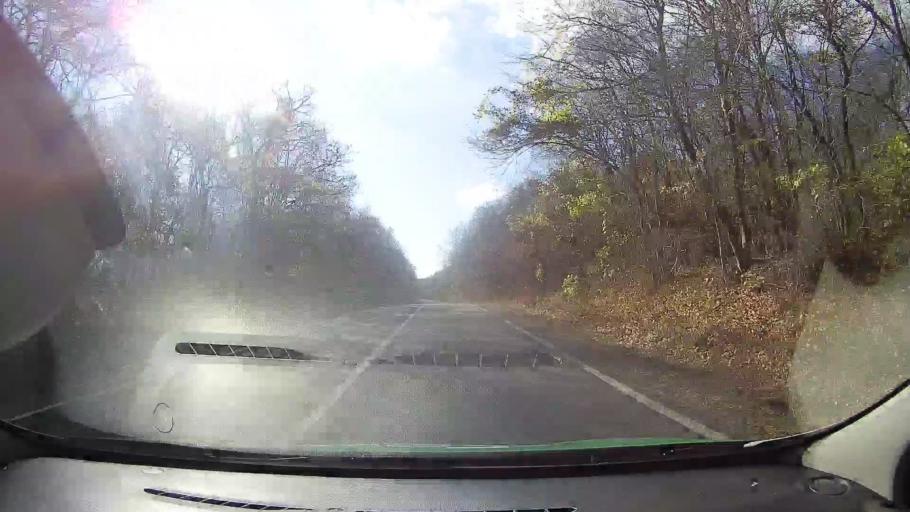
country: RO
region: Tulcea
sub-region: Oras Babadag
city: Babadag
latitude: 44.8416
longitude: 28.6972
